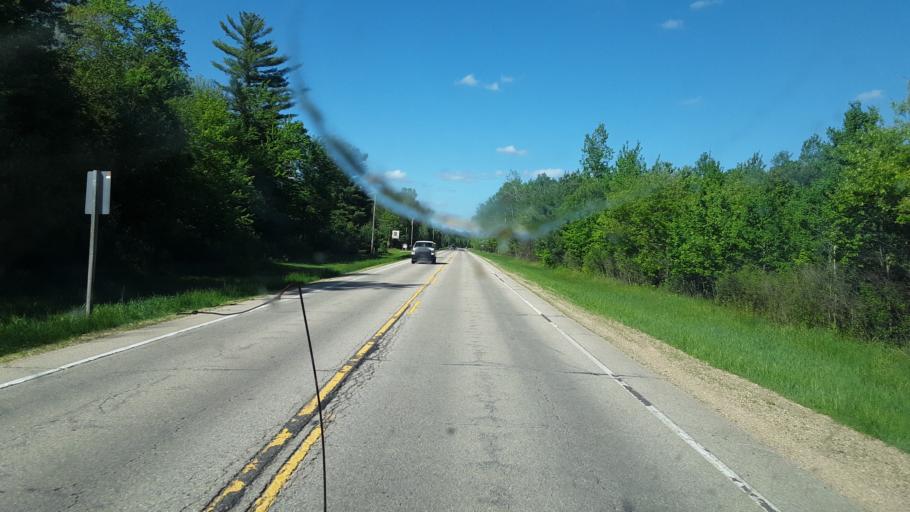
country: US
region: Wisconsin
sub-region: Juneau County
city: New Lisbon
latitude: 43.9112
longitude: -90.1259
